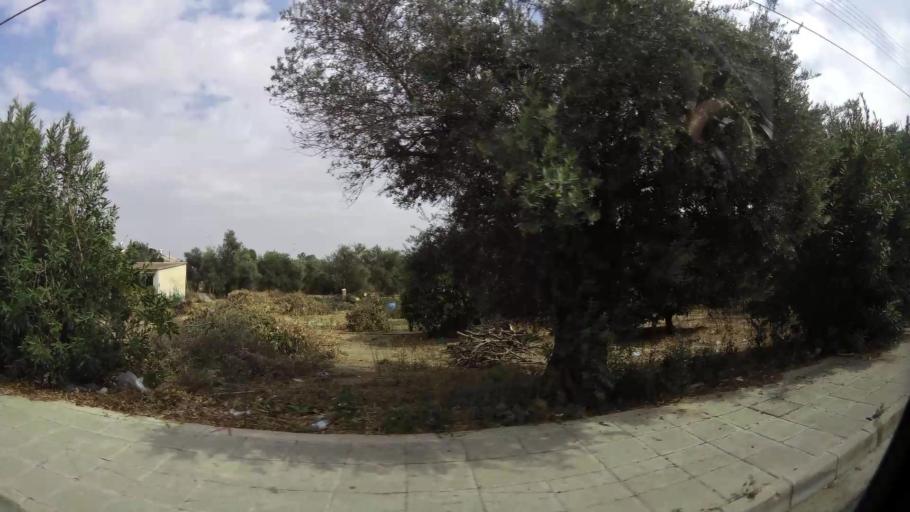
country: CY
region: Lefkosia
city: Geri
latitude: 35.1100
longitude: 33.3752
